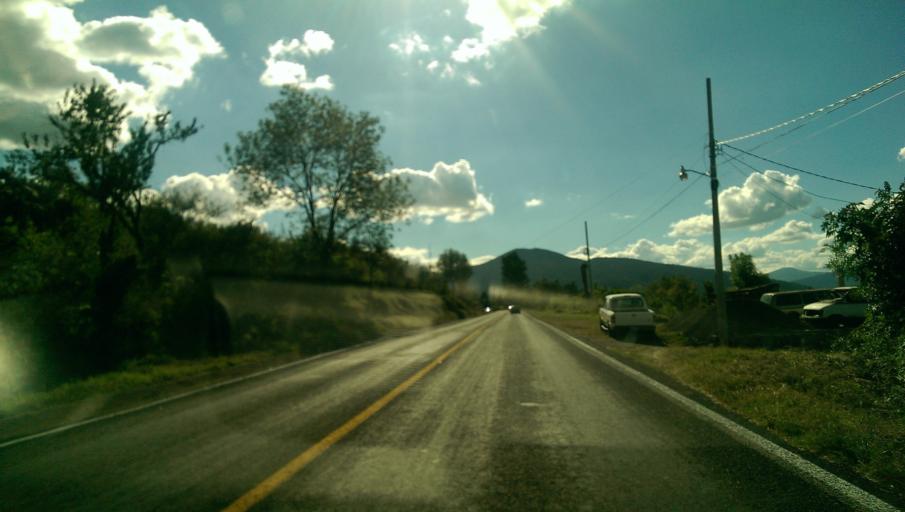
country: MX
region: Michoacan
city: Tzintzuntzan
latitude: 19.6399
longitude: -101.5471
